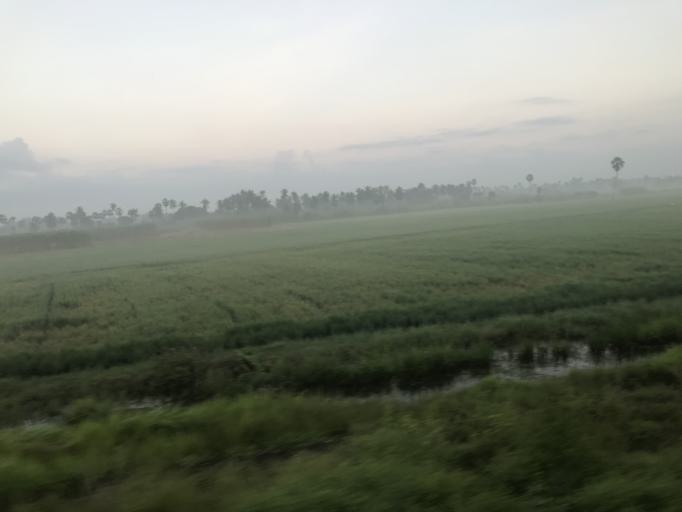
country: IN
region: Andhra Pradesh
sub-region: Guntur
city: Ponnur
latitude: 16.0826
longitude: 80.5641
